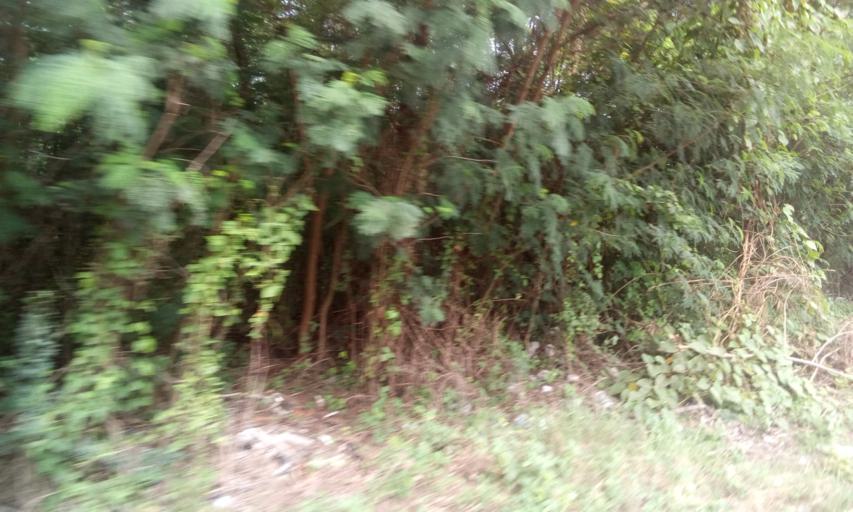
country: TH
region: Pathum Thani
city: Ban Lam Luk Ka
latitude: 14.0143
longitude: 100.8430
